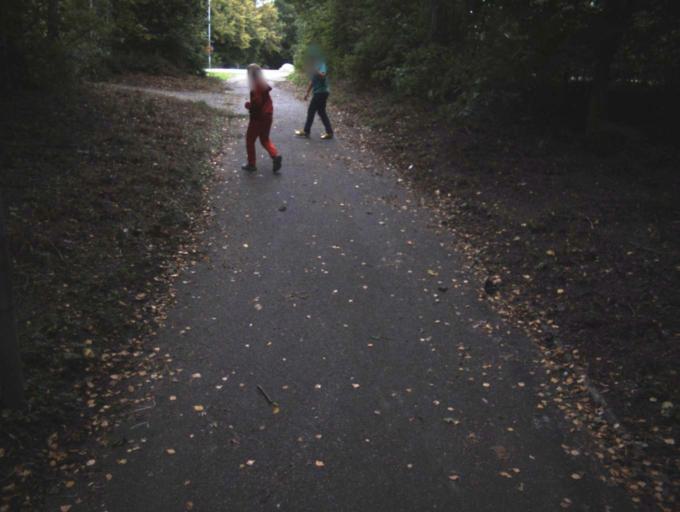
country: SE
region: Skane
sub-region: Helsingborg
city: Odakra
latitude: 56.1022
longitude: 12.7541
